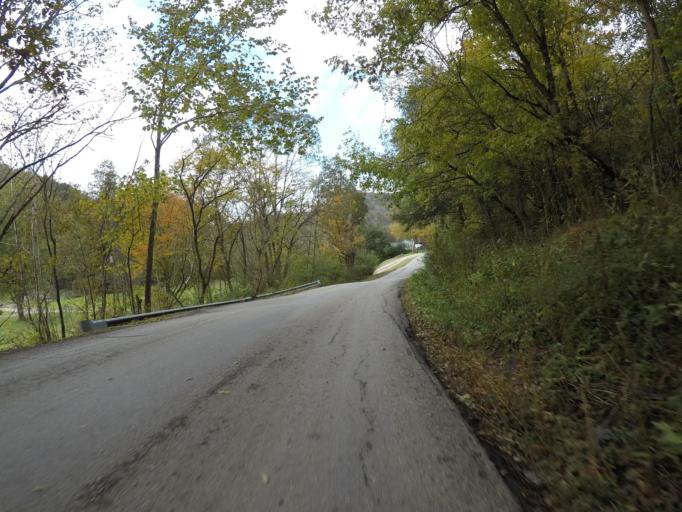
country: US
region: West Virginia
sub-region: Wayne County
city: Lavalette
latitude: 38.3363
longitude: -82.4464
